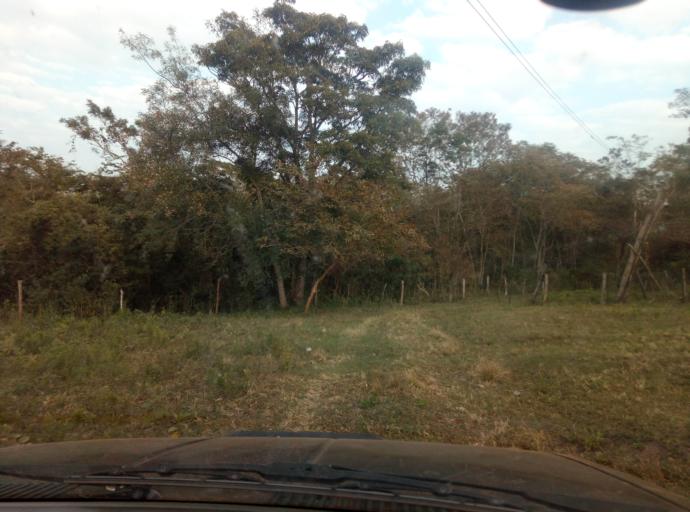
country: PY
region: Caaguazu
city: Doctor Cecilio Baez
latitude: -25.1872
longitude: -56.1293
